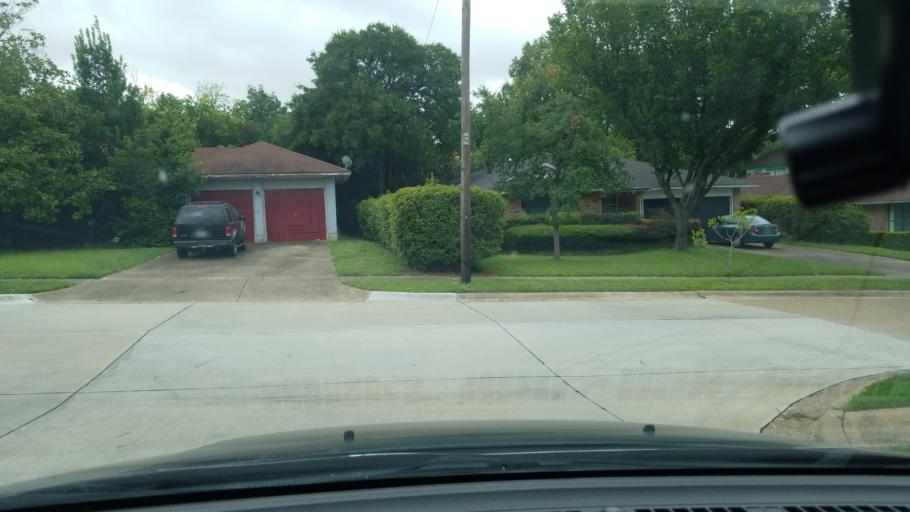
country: US
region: Texas
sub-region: Dallas County
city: Highland Park
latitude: 32.8108
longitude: -96.6966
